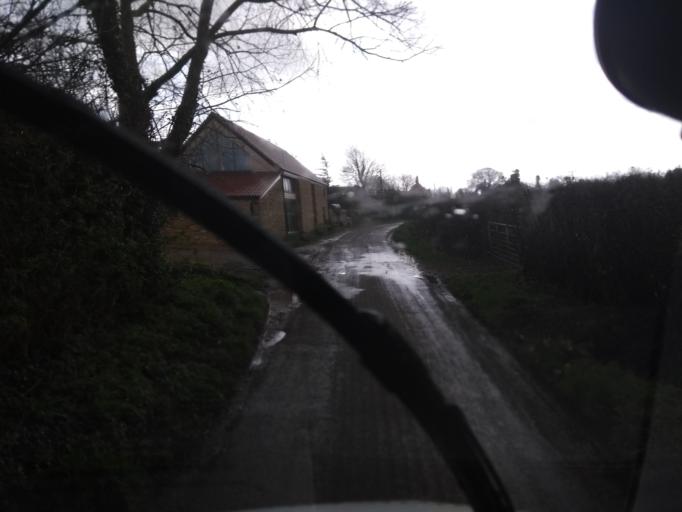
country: GB
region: England
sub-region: Somerset
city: South Petherton
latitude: 50.9721
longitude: -2.8109
